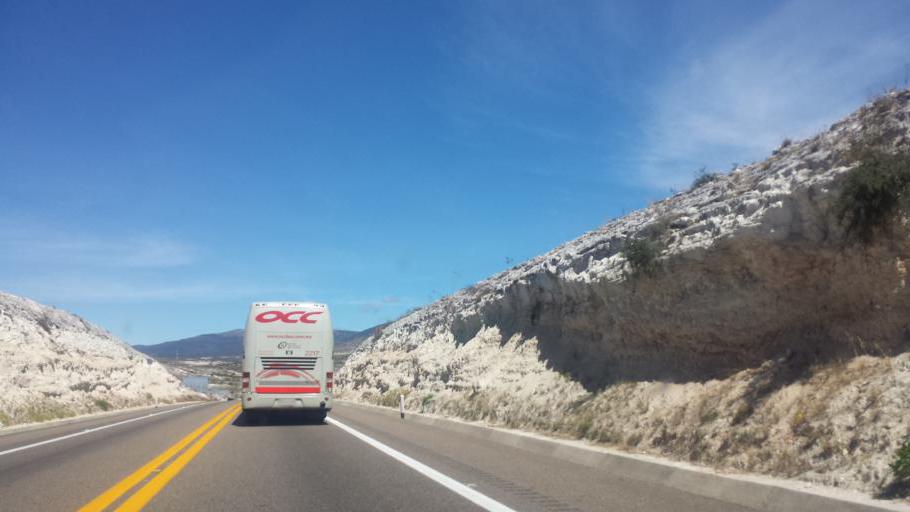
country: MX
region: Oaxaca
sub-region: Villa Tejupam de la Union
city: Villa Tejupam de la Union
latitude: 17.8936
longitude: -97.3701
